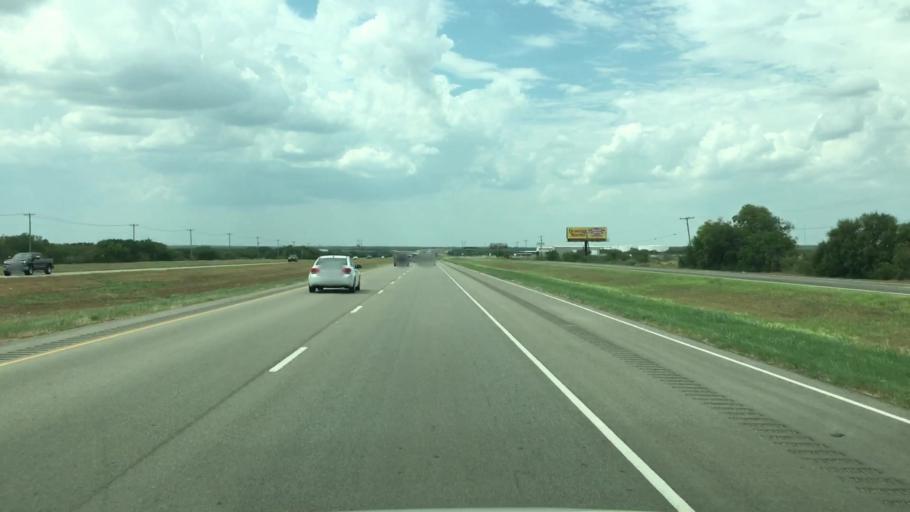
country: US
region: Texas
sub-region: Live Oak County
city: Three Rivers
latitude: 28.5056
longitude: -98.1621
